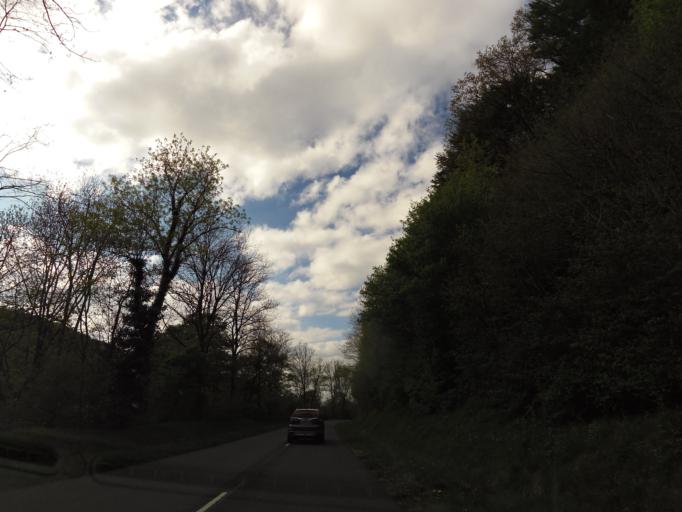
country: FR
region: Midi-Pyrenees
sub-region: Departement du Tarn
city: Soreze
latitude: 43.4237
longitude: 2.0577
